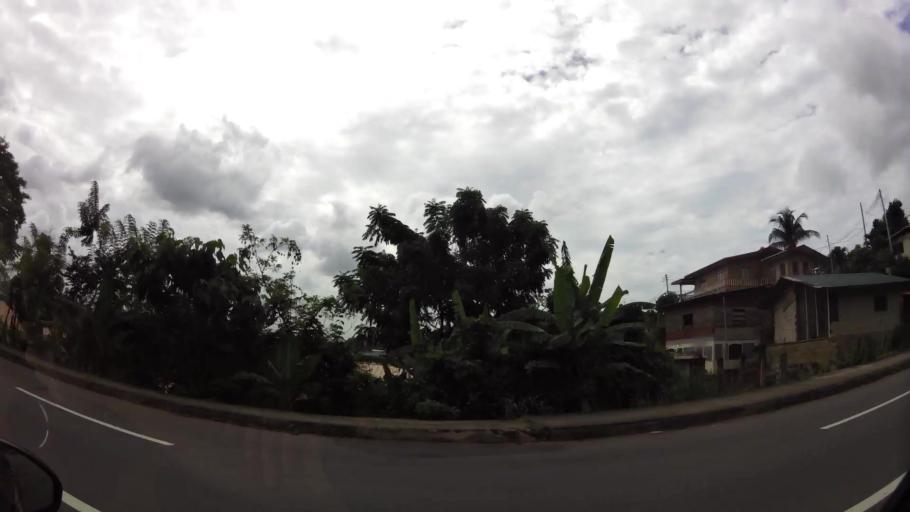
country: TT
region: San Juan/Laventille
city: Laventille
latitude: 10.6660
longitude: -61.4807
